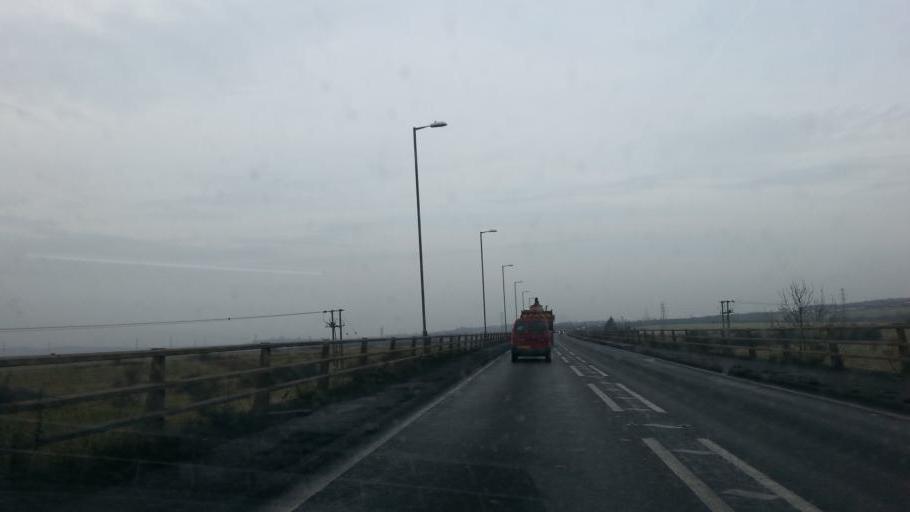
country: GB
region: England
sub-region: Essex
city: South Benfleet
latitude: 51.5441
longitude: 0.5467
